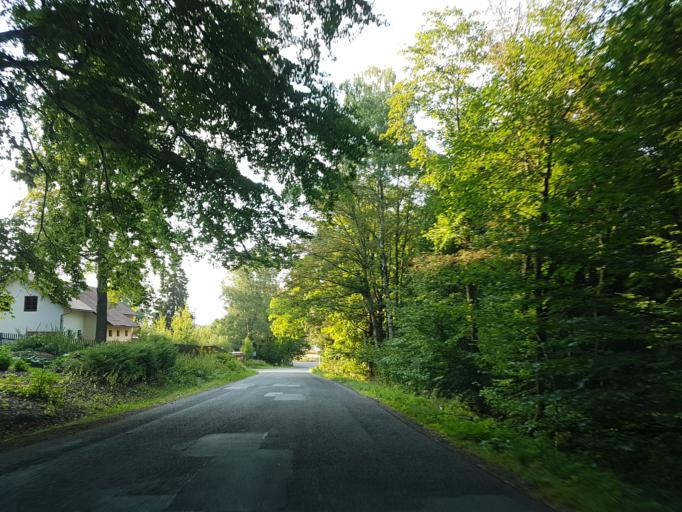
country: CZ
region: Liberecky
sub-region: Okres Jablonec nad Nisou
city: Jablonec nad Nisou
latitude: 50.7150
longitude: 15.1885
